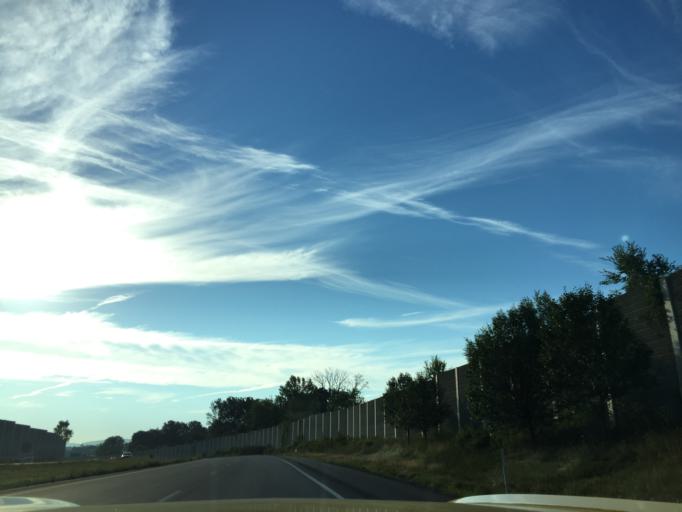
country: US
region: Pennsylvania
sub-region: Lehigh County
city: Wescosville
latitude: 40.5639
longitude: -75.5741
